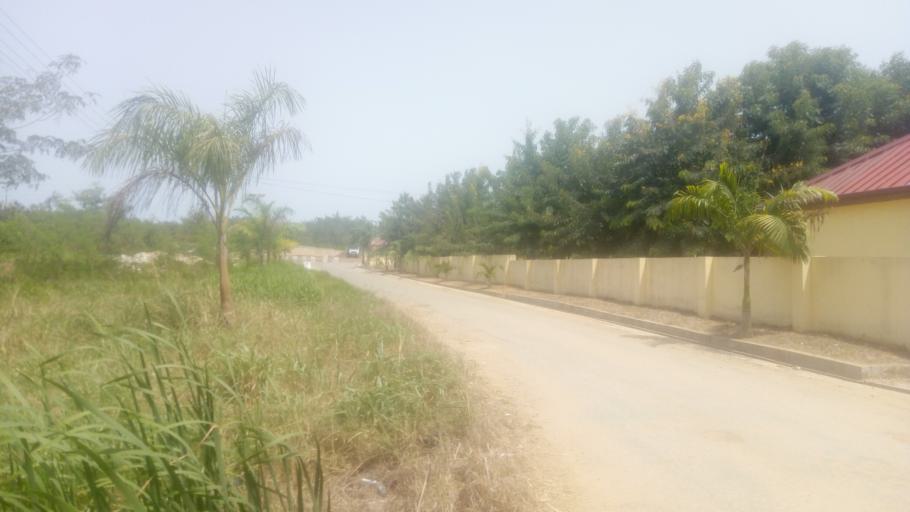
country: GH
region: Central
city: Winneba
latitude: 5.3688
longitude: -0.6297
